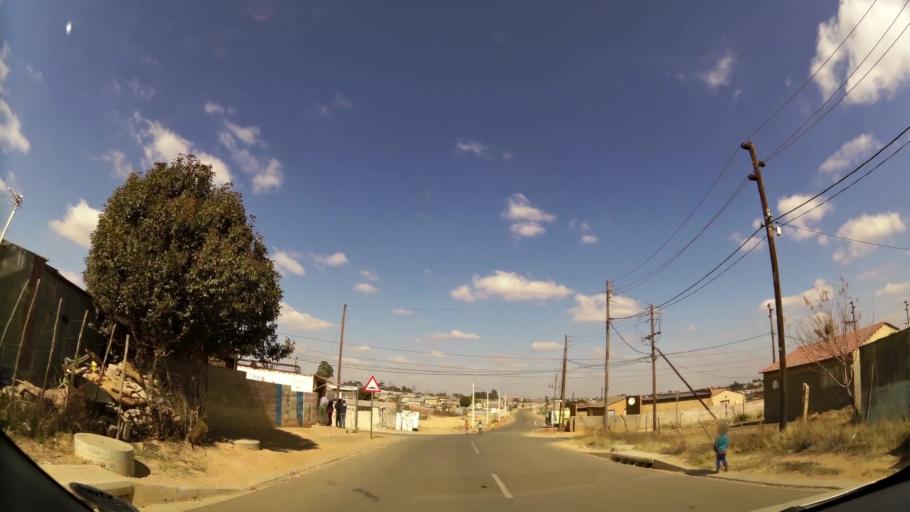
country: ZA
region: Gauteng
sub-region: West Rand District Municipality
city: Krugersdorp
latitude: -26.1388
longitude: 27.7901
